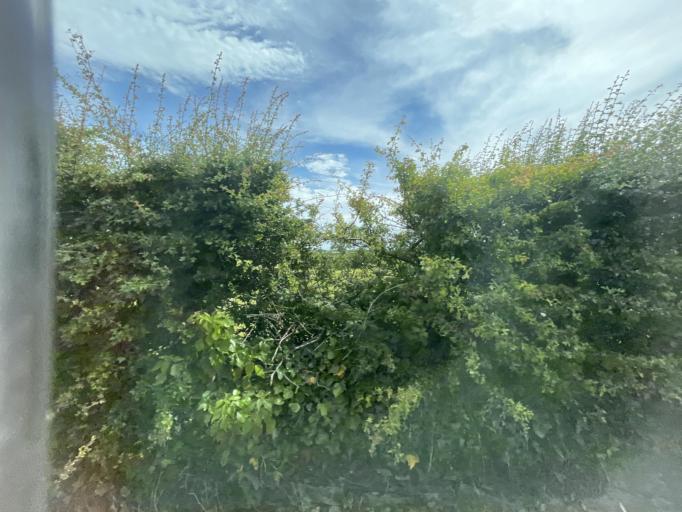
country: GB
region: Wales
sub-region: Anglesey
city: Llanfachraeth
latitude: 53.2684
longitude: -4.4704
